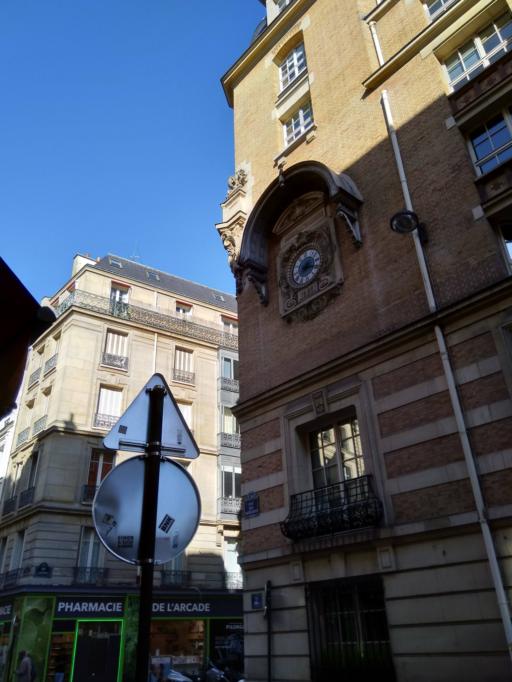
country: FR
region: Ile-de-France
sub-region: Paris
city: Saint-Ouen
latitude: 48.8733
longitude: 2.3245
